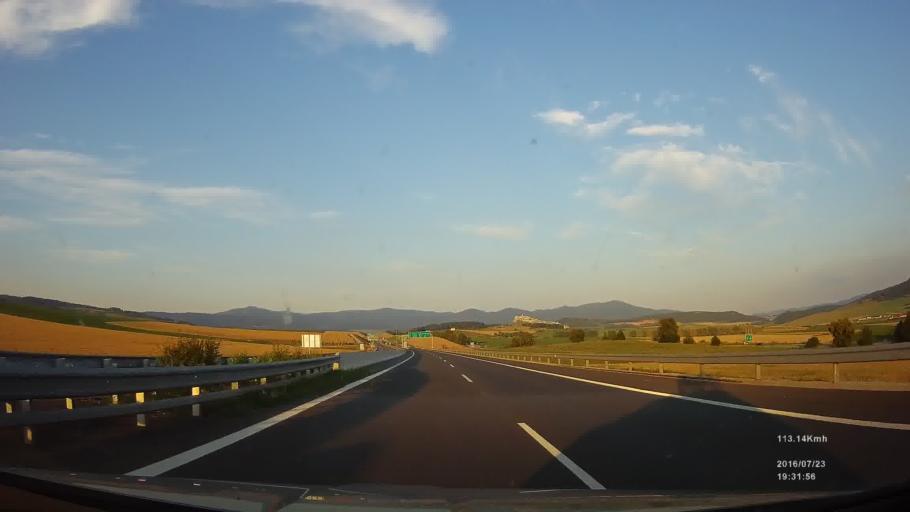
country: SK
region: Presovsky
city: Spisske Podhradie
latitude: 49.0062
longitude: 20.6941
